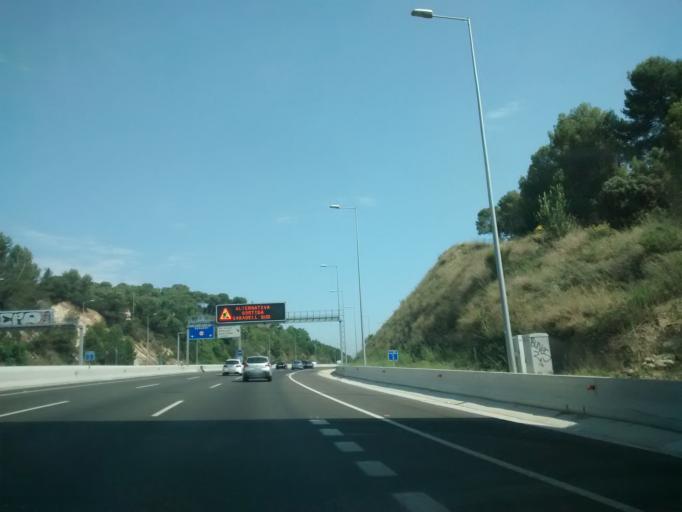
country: ES
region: Catalonia
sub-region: Provincia de Barcelona
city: Montcada i Reixac
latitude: 41.4728
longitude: 2.1635
